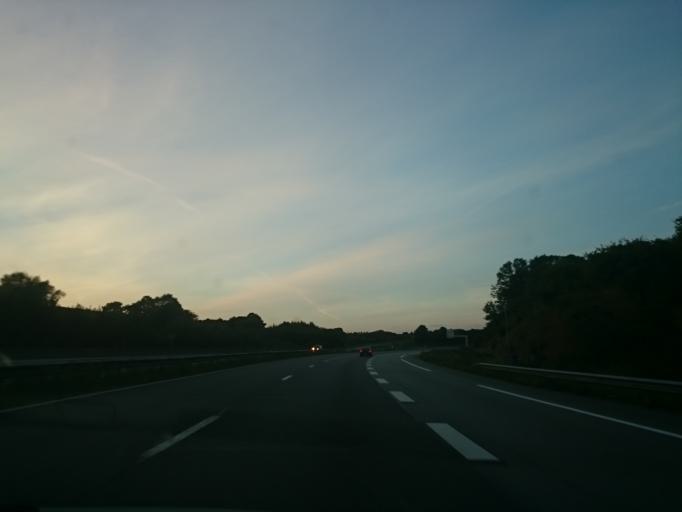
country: FR
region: Brittany
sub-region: Departement du Finistere
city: Quimper
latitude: 48.0257
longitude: -4.0857
